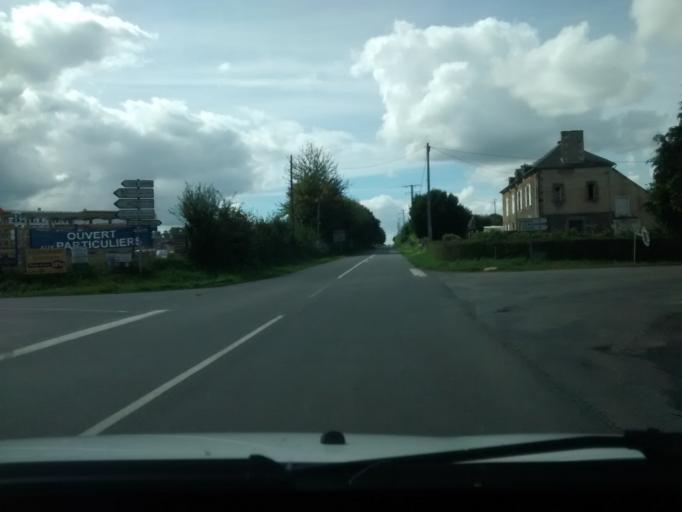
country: FR
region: Brittany
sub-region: Departement d'Ille-et-Vilaine
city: Tinteniac
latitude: 48.3246
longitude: -1.8522
